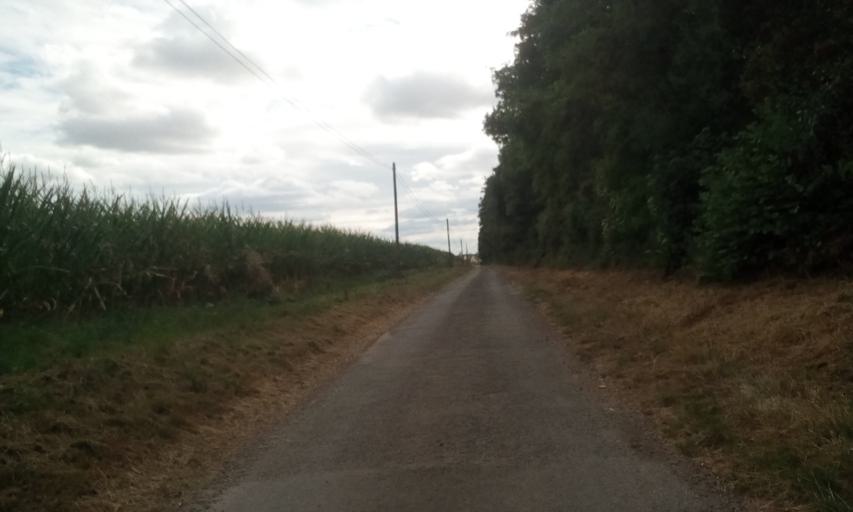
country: FR
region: Lower Normandy
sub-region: Departement du Calvados
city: Bellengreville
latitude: 49.1283
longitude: -0.1941
